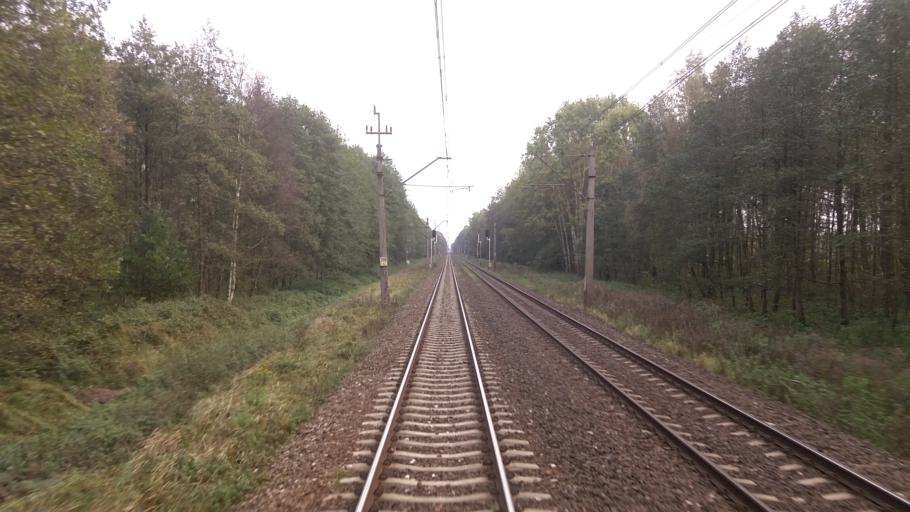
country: PL
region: West Pomeranian Voivodeship
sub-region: Powiat stargardzki
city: Kobylanka
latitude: 53.3772
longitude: 14.8200
